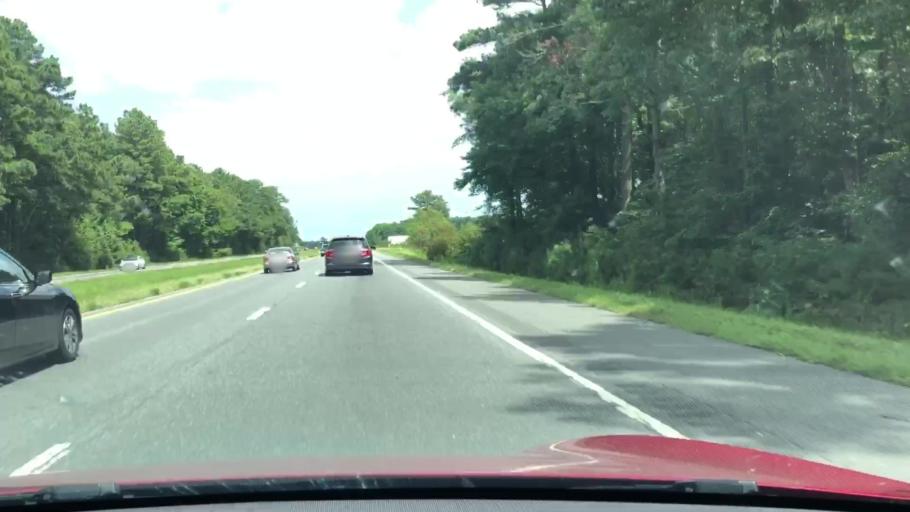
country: US
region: Virginia
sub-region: Accomack County
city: Accomac
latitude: 37.7280
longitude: -75.6678
